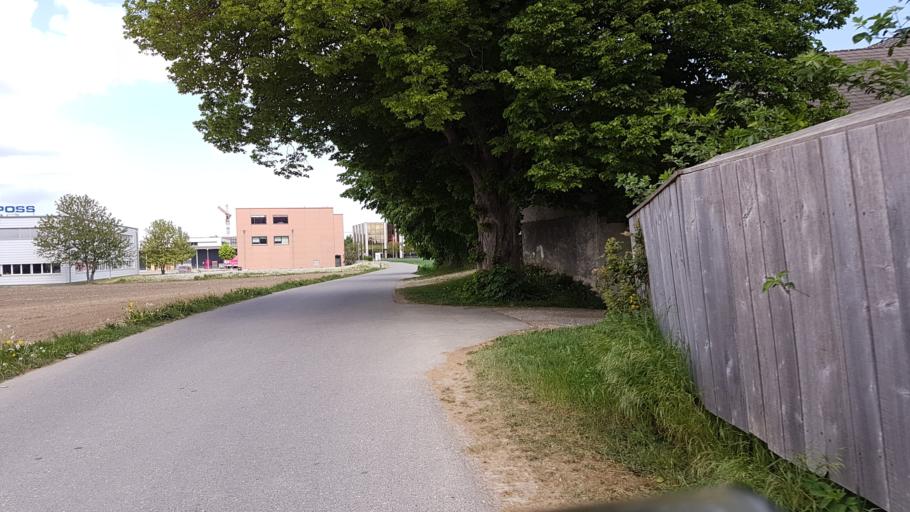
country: CH
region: Bern
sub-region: Bern-Mittelland District
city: Belp
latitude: 46.8992
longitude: 7.5059
